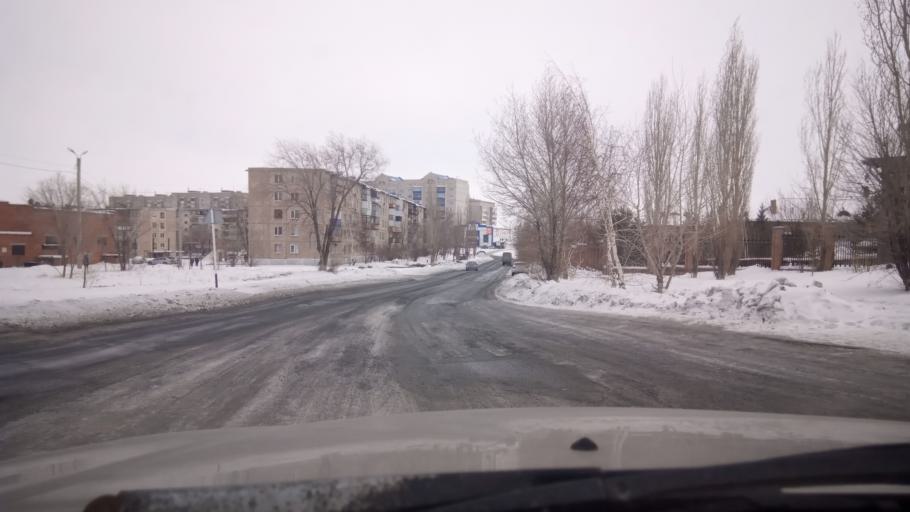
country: RU
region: Orenburg
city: Novotroitsk
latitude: 51.1902
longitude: 58.2710
